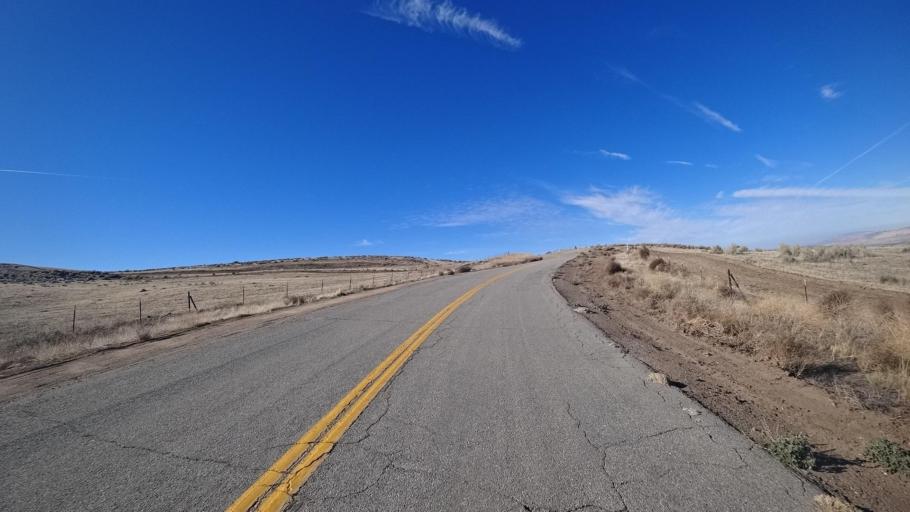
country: US
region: California
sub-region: Kern County
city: Maricopa
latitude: 34.9344
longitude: -119.4122
